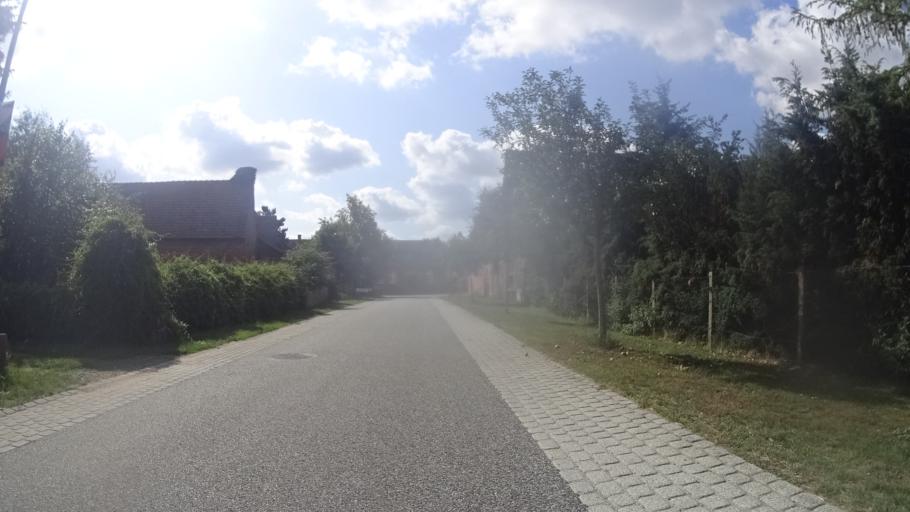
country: DE
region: Brandenburg
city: Ruhstadt
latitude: 52.9215
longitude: 11.8709
